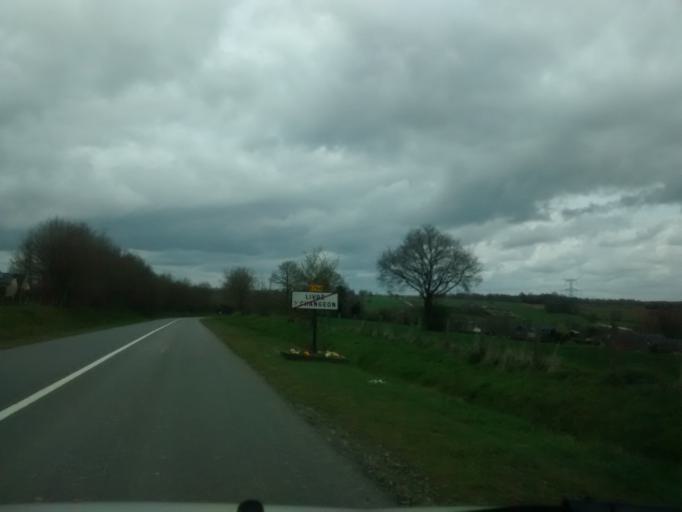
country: FR
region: Brittany
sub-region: Departement d'Ille-et-Vilaine
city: Livre-sur-Changeon
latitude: 48.2238
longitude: -1.3494
